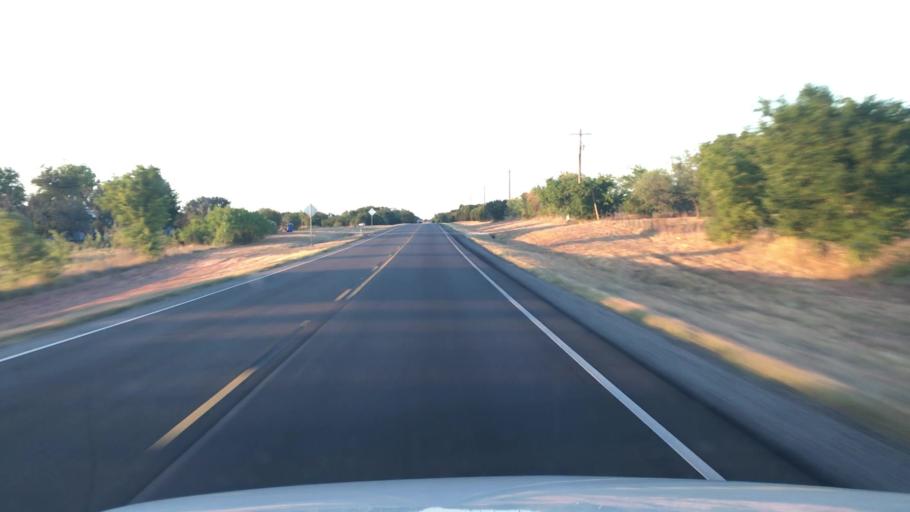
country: US
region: Texas
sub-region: Hamilton County
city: Hico
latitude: 32.0479
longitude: -98.0024
